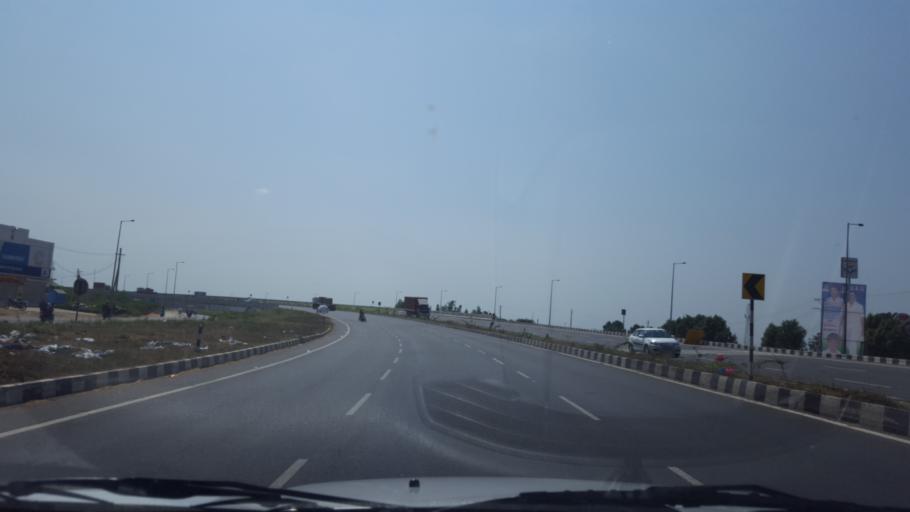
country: IN
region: Andhra Pradesh
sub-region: Prakasam
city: Ongole
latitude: 15.5368
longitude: 80.0504
